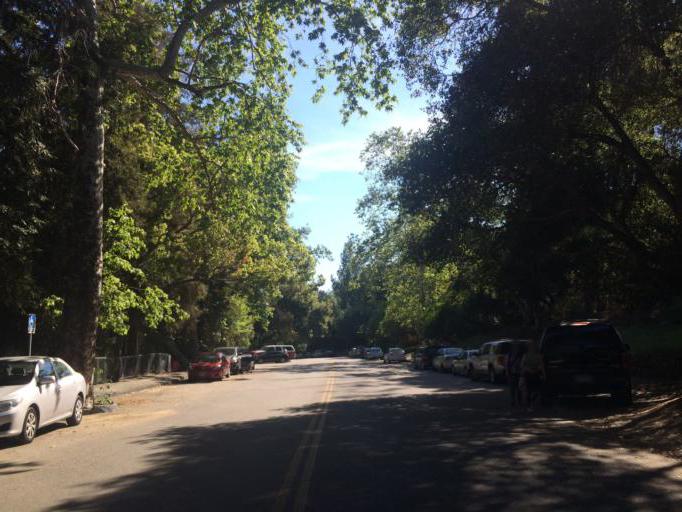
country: US
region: California
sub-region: Los Angeles County
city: Hollywood
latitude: 34.1146
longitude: -118.3072
